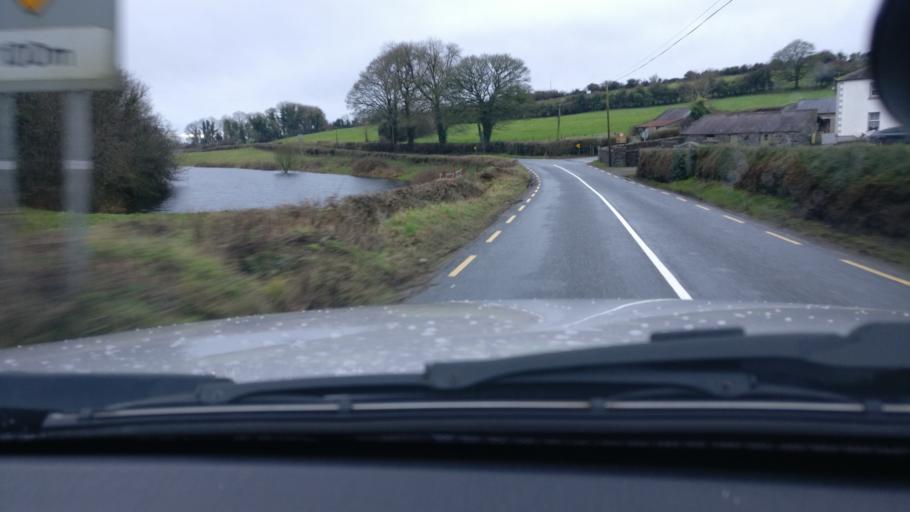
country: IE
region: Leinster
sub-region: An Longfort
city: Granard
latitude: 53.8025
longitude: -7.3878
